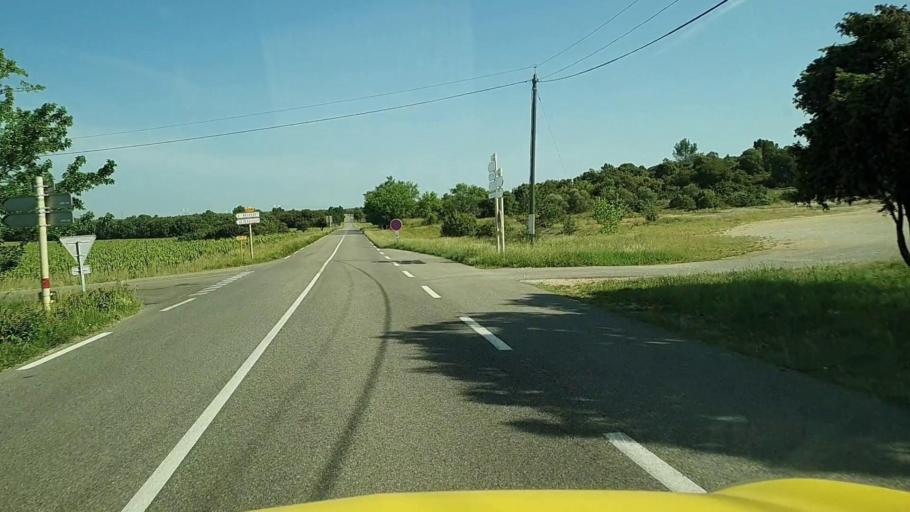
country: FR
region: Languedoc-Roussillon
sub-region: Departement du Gard
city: Montaren-et-Saint-Mediers
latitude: 44.0846
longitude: 4.3909
